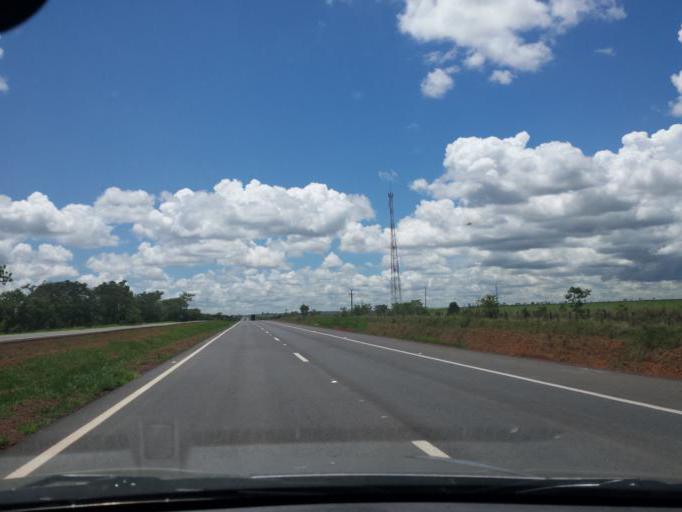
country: BR
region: Goias
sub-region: Cristalina
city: Cristalina
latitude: -16.6755
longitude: -47.7092
